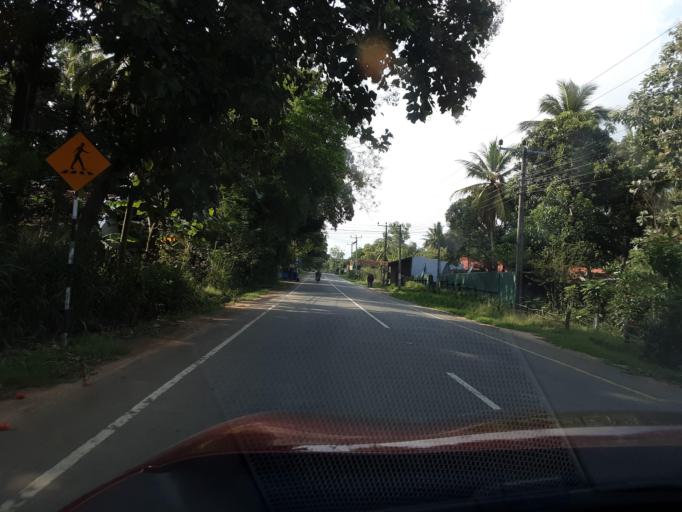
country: LK
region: Uva
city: Haputale
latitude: 6.6729
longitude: 81.1124
